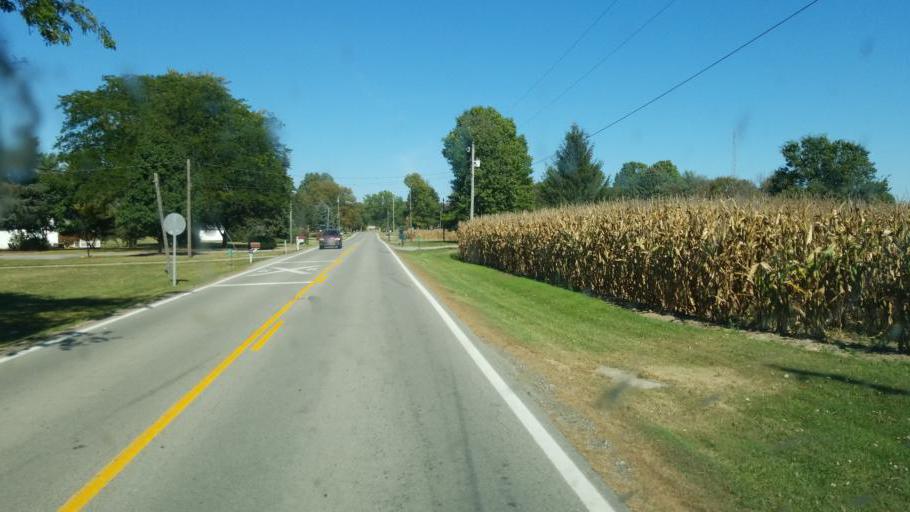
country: US
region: Ohio
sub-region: Huron County
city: Plymouth
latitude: 41.0248
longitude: -82.6853
